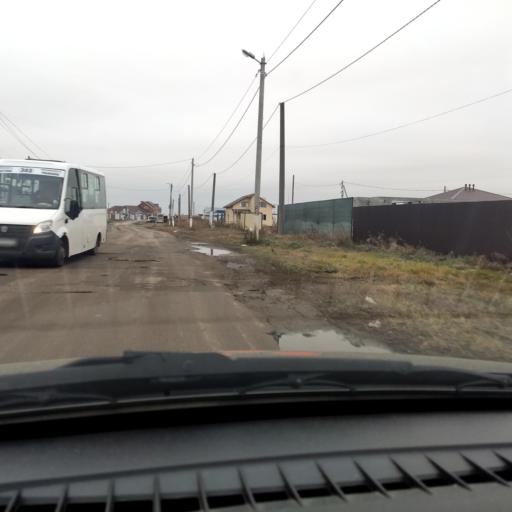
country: RU
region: Samara
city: Podstepki
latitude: 53.5148
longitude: 49.2215
